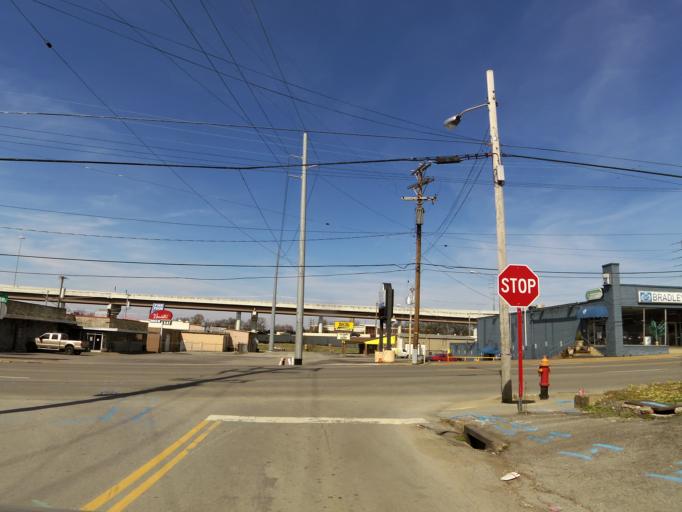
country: US
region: Tennessee
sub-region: Davidson County
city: Belle Meade
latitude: 36.1517
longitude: -86.8512
